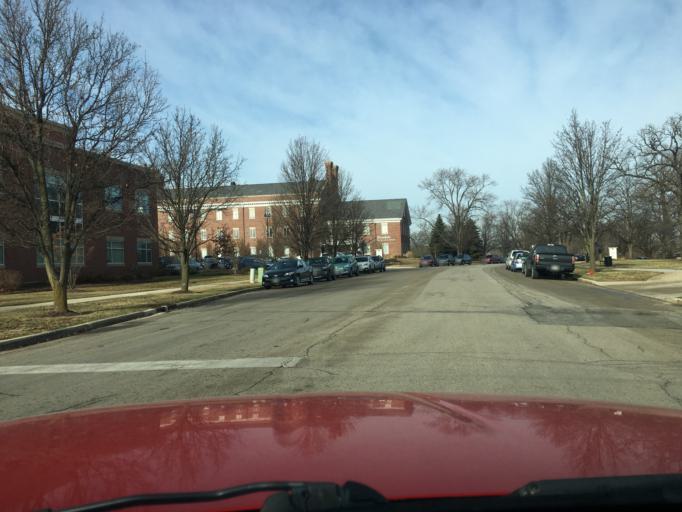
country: US
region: Illinois
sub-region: DuPage County
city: Oak Brook
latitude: 41.8185
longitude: -87.9214
